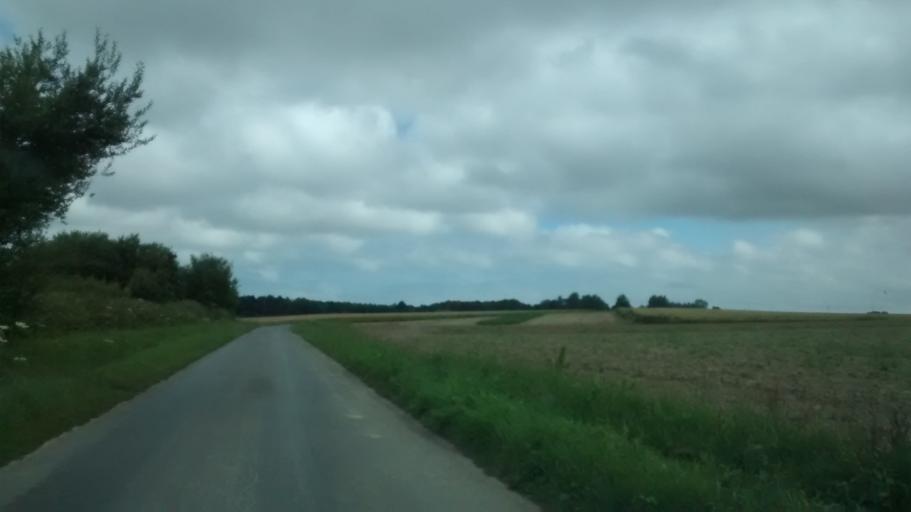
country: FR
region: Brittany
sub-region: Departement d'Ille-et-Vilaine
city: Saint-Meloir-des-Ondes
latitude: 48.6430
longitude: -1.9127
